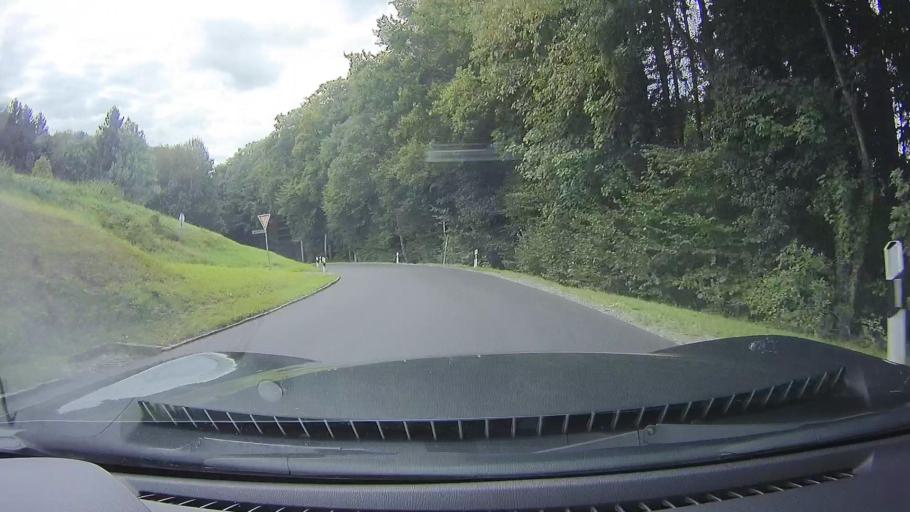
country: DE
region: Baden-Wuerttemberg
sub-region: Regierungsbezirk Stuttgart
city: Althutte
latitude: 48.9115
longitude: 9.5491
